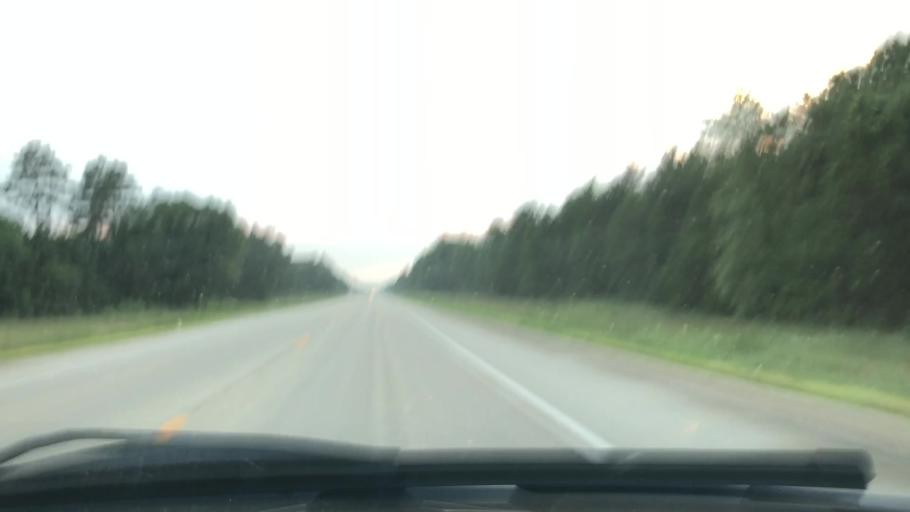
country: US
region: Wisconsin
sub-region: Sauk County
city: Spring Green
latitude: 43.1912
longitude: -90.1825
